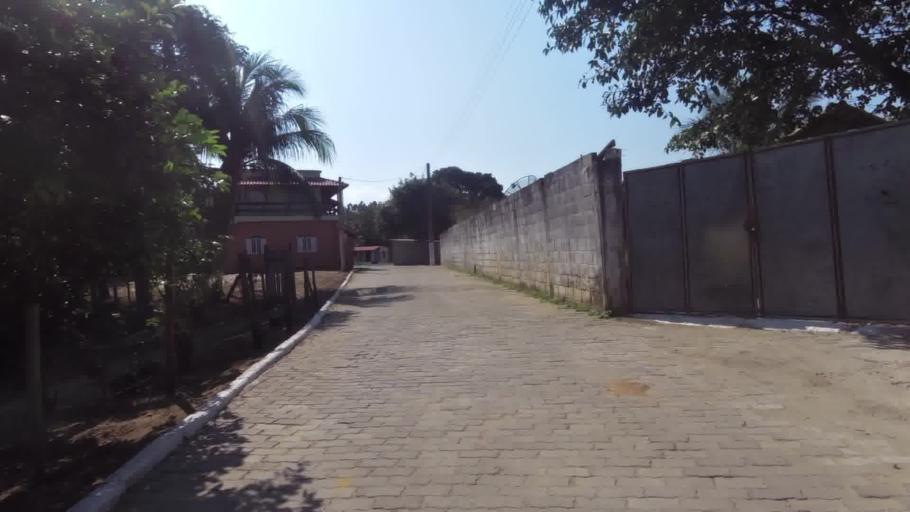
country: BR
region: Espirito Santo
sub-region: Piuma
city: Piuma
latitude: -20.8073
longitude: -40.7384
